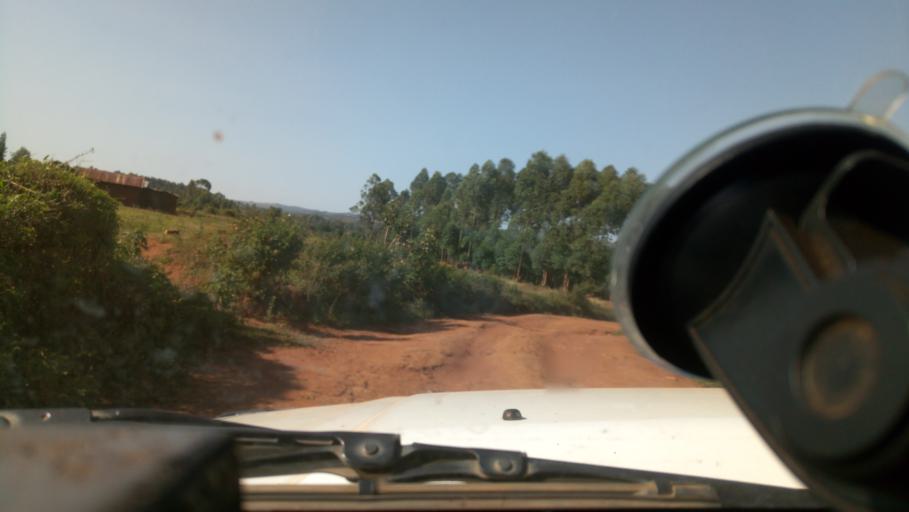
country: TZ
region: Mara
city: Sirari
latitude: -1.2322
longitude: 34.5312
